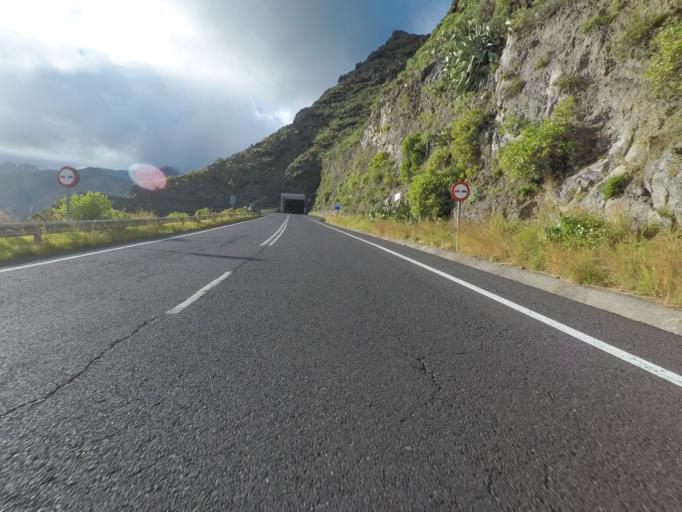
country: ES
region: Canary Islands
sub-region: Provincia de Santa Cruz de Tenerife
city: Hermigua
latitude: 28.1244
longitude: -17.1604
